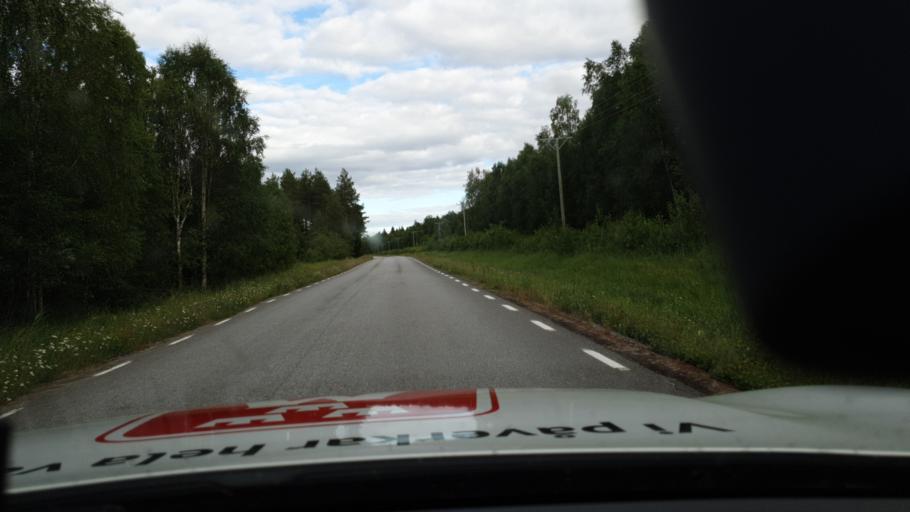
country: SE
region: Norrbotten
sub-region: Kalix Kommun
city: Toere
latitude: 65.8940
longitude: 22.6346
